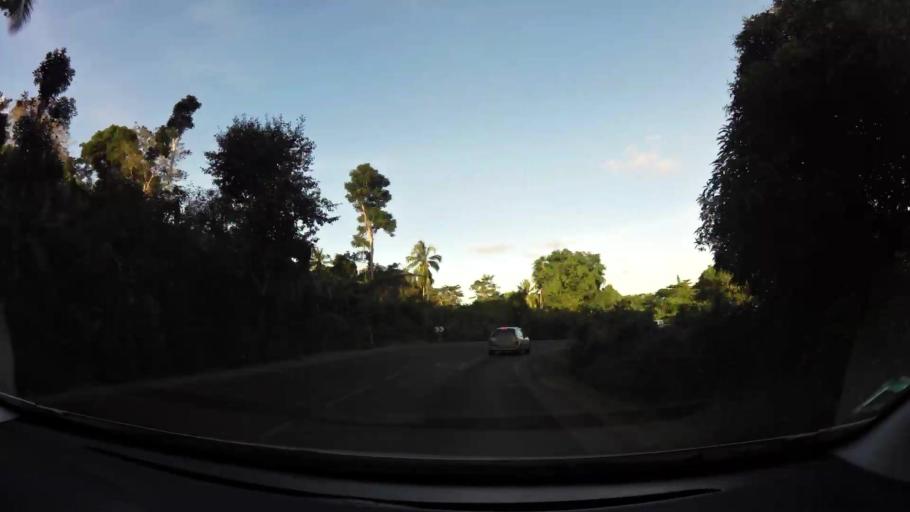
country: YT
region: Dembeni
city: Dembeni
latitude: -12.8375
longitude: 45.1801
